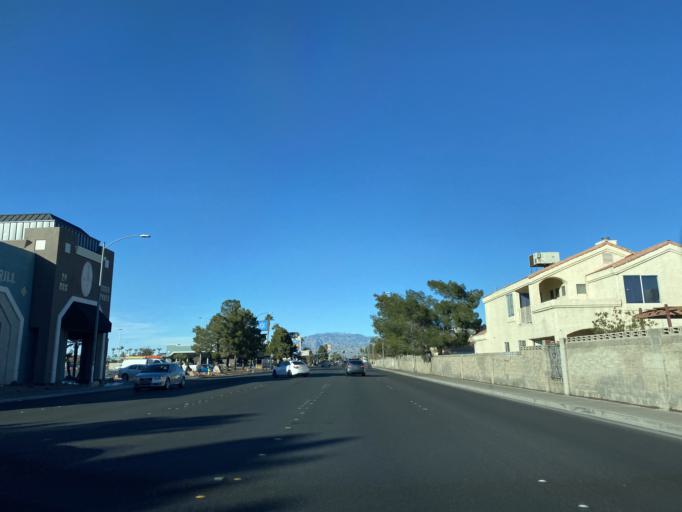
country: US
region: Nevada
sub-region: Clark County
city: Spring Valley
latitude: 36.2137
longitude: -115.2423
